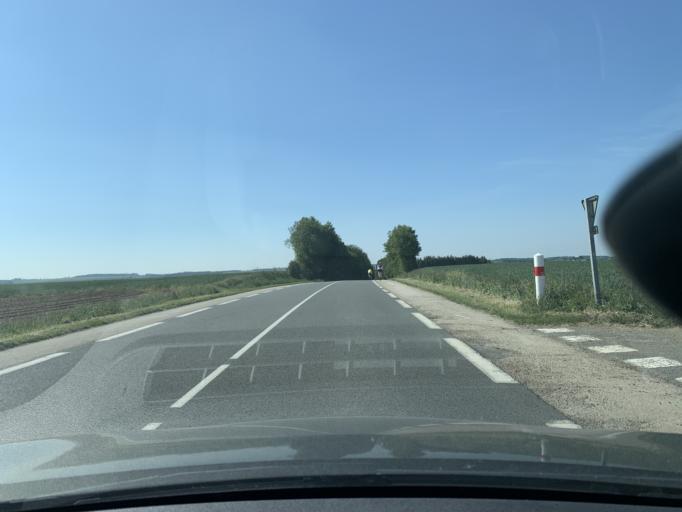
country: FR
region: Nord-Pas-de-Calais
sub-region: Departement du Nord
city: Rumilly-en-Cambresis
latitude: 50.1182
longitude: 3.2461
